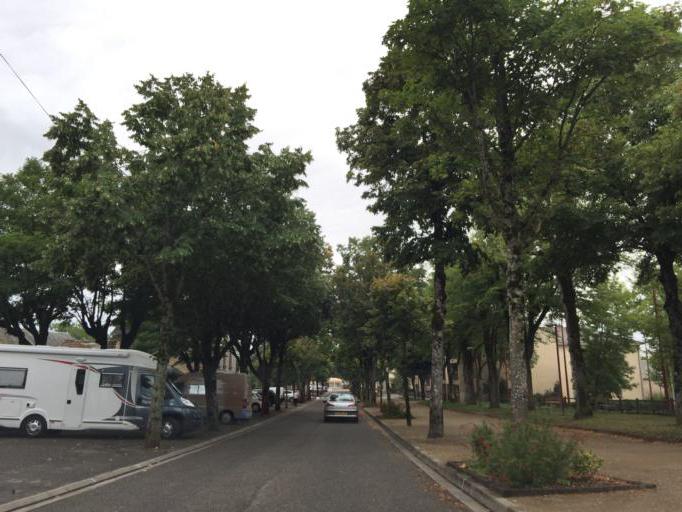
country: FR
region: Midi-Pyrenees
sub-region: Departement de l'Aveyron
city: Bozouls
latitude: 44.4712
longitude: 2.7225
